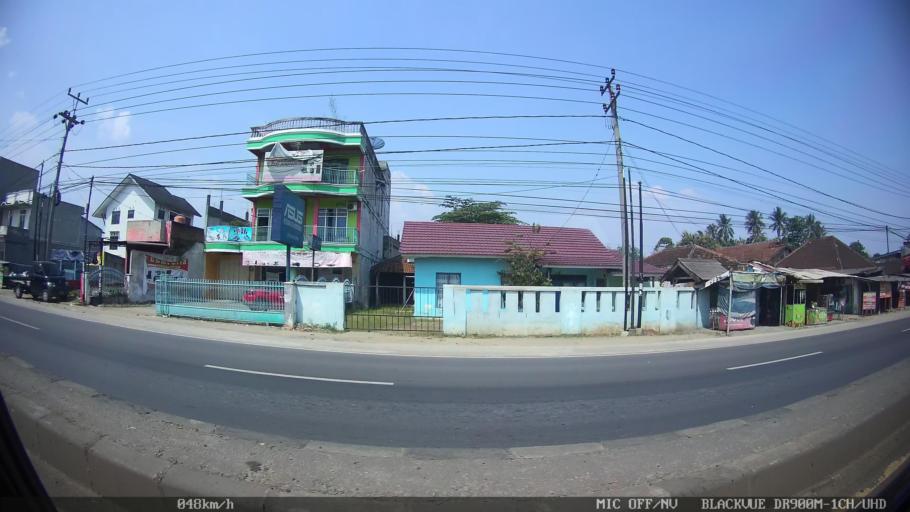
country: ID
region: Lampung
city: Natar
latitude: -5.3140
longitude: 105.1966
